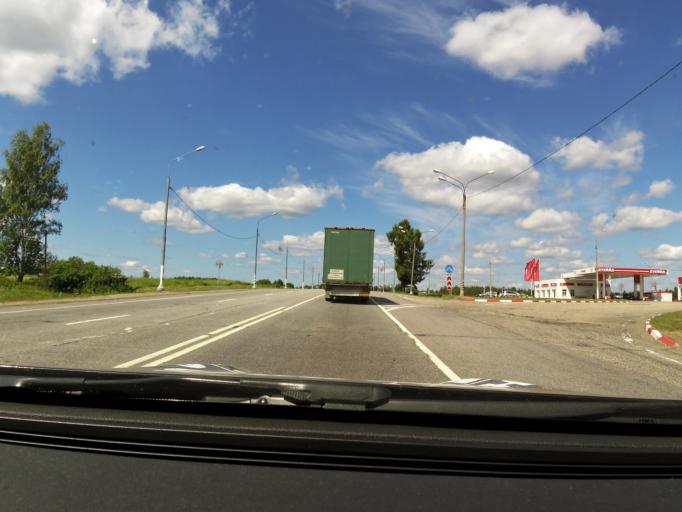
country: RU
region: Tverskaya
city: Kuzhenkino
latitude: 57.7823
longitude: 33.9070
